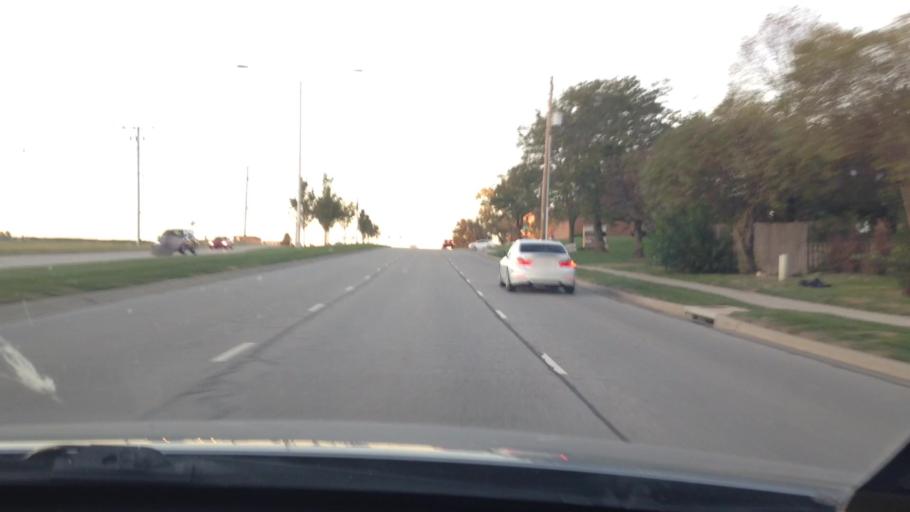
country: US
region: Kansas
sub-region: Johnson County
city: Lenexa
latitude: 38.9247
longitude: -94.7235
